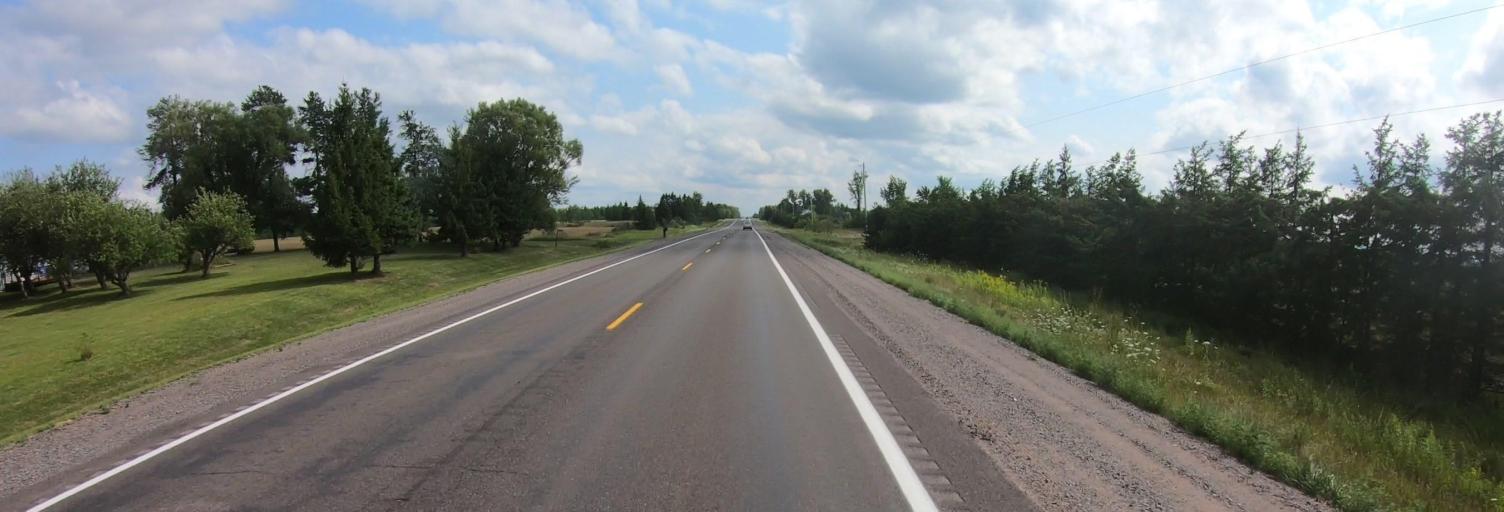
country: US
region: Michigan
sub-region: Ontonagon County
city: Ontonagon
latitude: 46.5882
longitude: -89.1785
